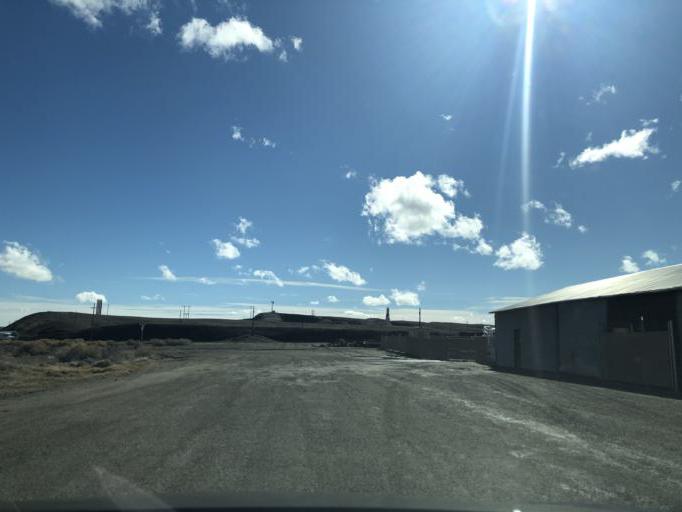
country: US
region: Utah
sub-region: Carbon County
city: East Carbon City
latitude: 38.9950
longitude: -110.1688
